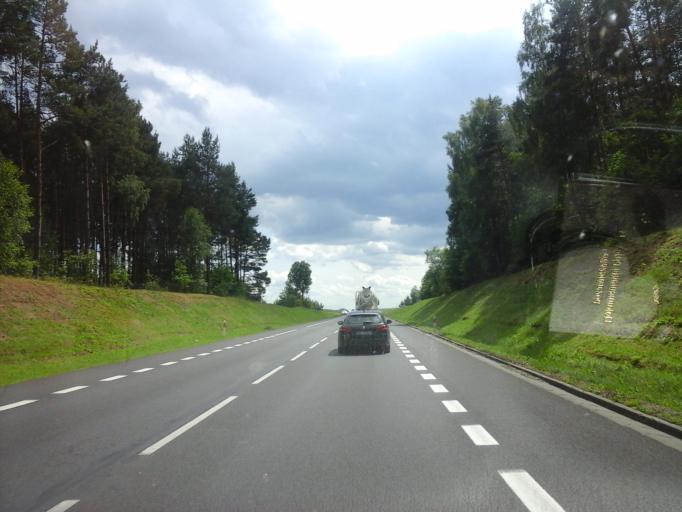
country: PL
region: West Pomeranian Voivodeship
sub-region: Powiat bialogardzki
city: Karlino
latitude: 54.0419
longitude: 15.8982
